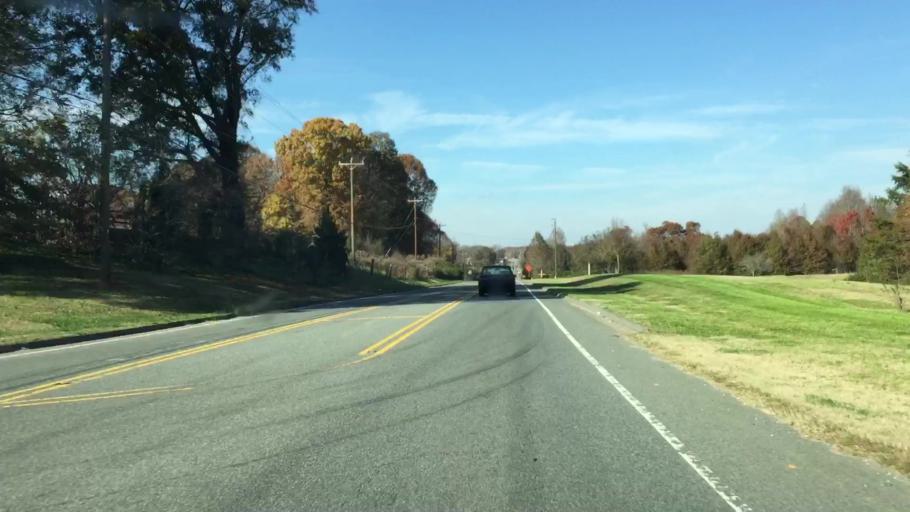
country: US
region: North Carolina
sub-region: Iredell County
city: Troutman
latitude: 35.6594
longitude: -80.8487
